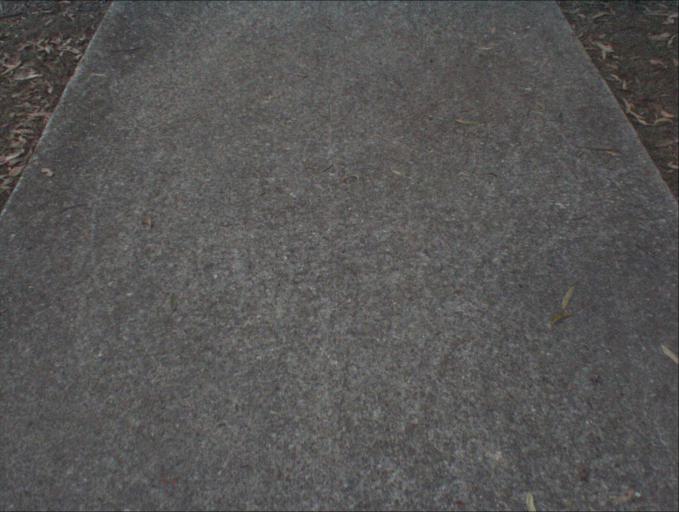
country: AU
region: Queensland
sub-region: Logan
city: Park Ridge South
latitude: -27.6779
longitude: 153.0186
